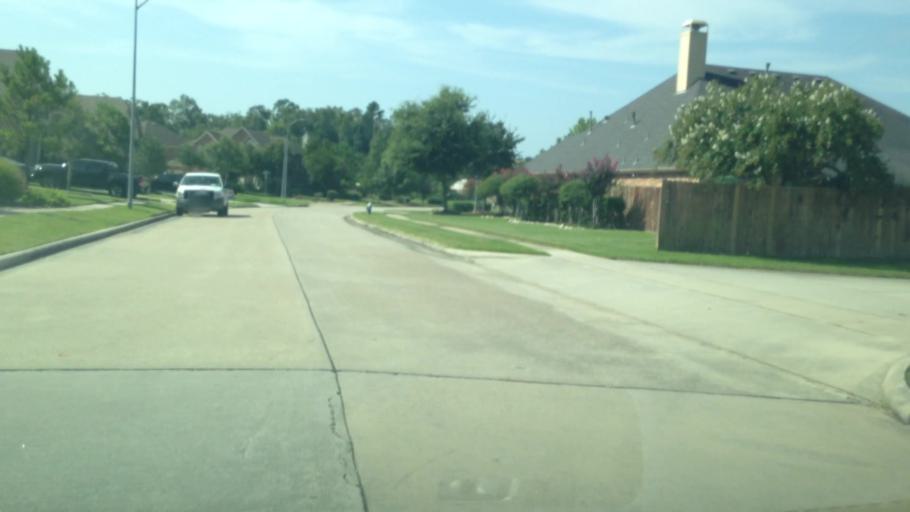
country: US
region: Texas
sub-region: Harris County
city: Sheldon
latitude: 29.9206
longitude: -95.1710
